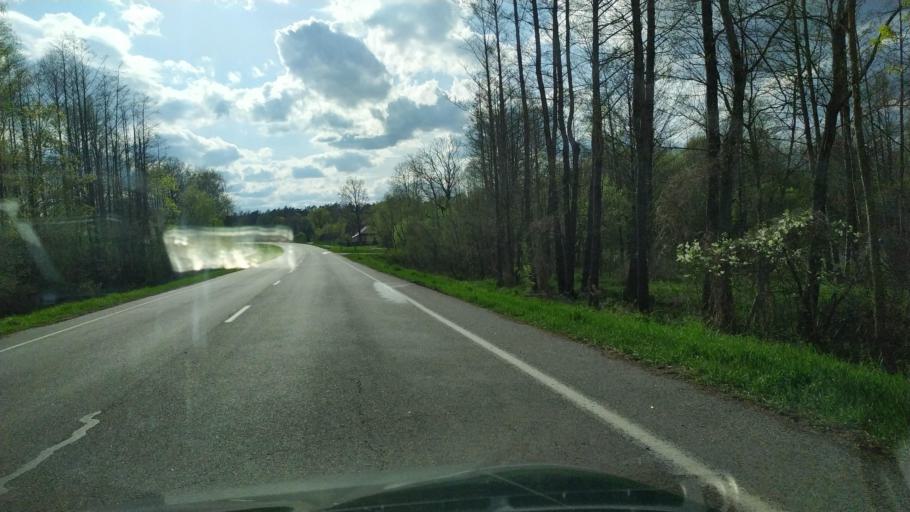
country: BY
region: Brest
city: Pruzhany
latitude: 52.7036
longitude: 24.3204
